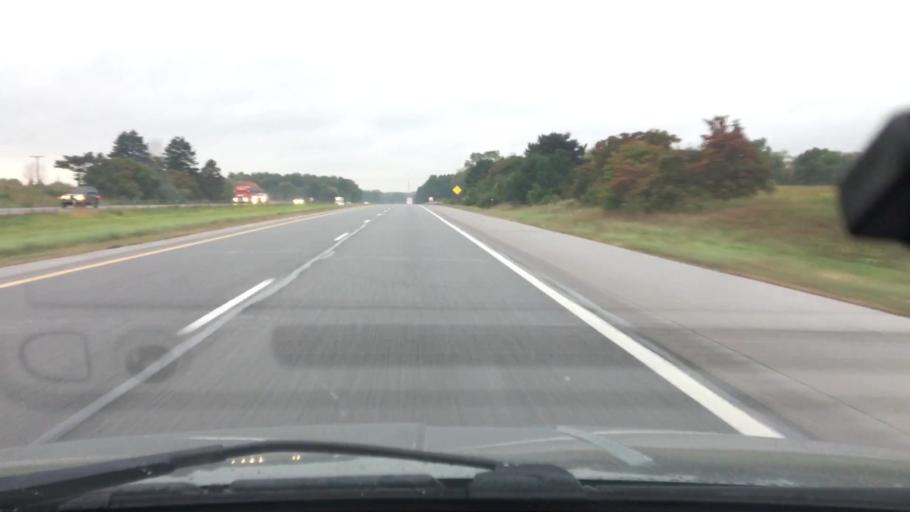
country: US
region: Michigan
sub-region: Washtenaw County
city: Dexter
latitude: 42.2977
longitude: -83.9327
